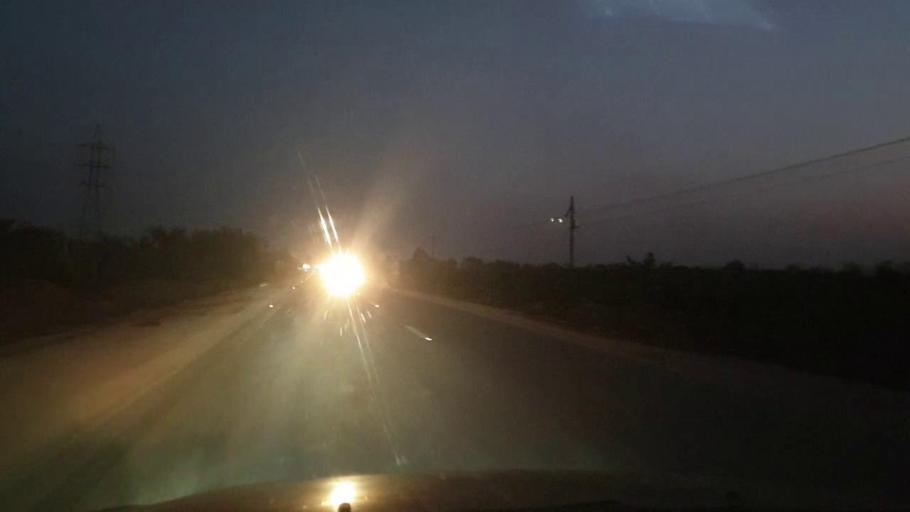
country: PK
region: Sindh
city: Chambar
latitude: 25.3604
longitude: 68.7862
